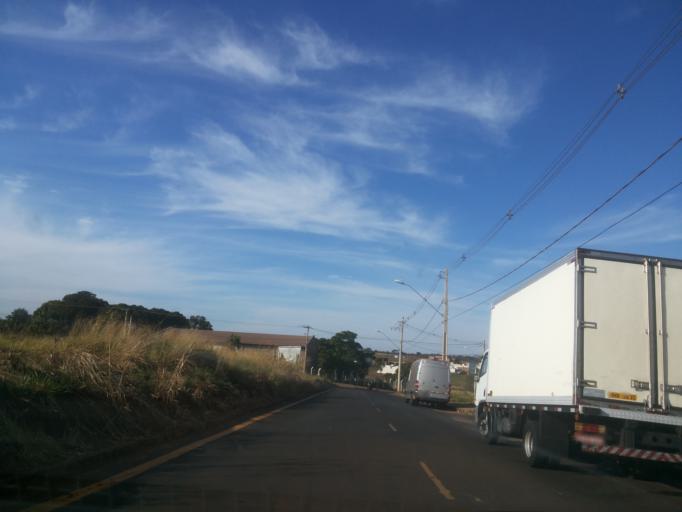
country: BR
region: Minas Gerais
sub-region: Ituiutaba
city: Ituiutaba
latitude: -18.9954
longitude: -49.4665
